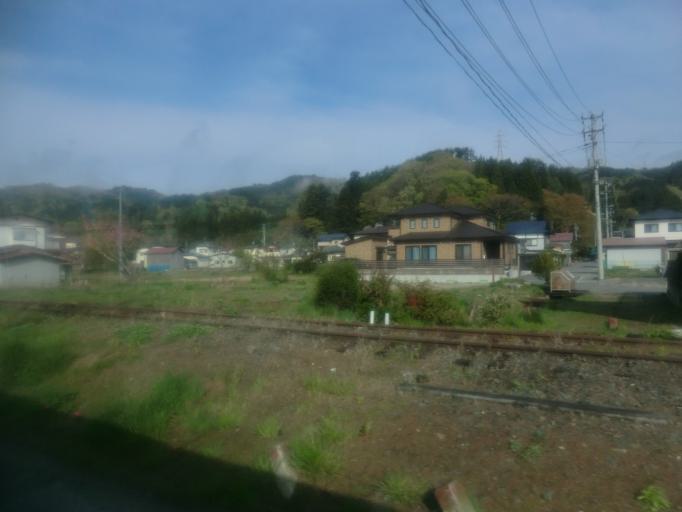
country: JP
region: Iwate
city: Miyako
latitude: 39.5826
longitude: 141.9387
